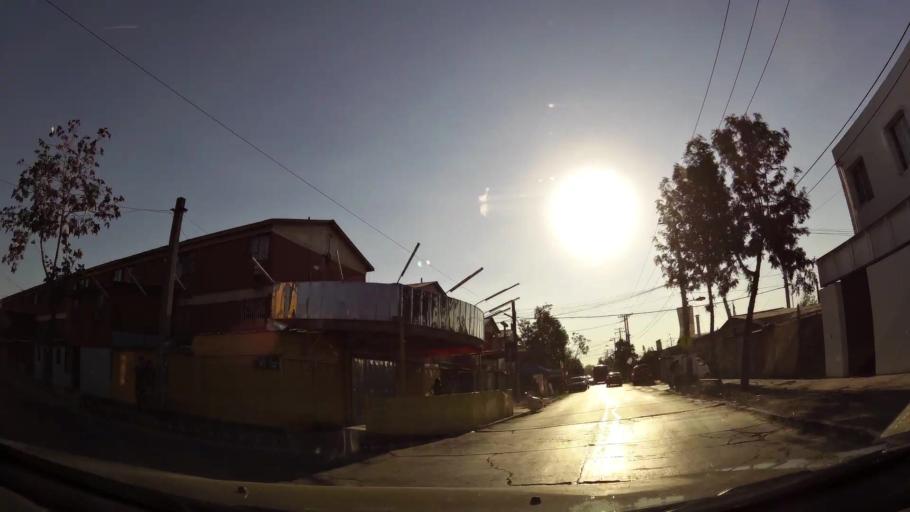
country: CL
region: Santiago Metropolitan
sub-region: Provincia de Santiago
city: La Pintana
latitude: -33.5774
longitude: -70.6634
